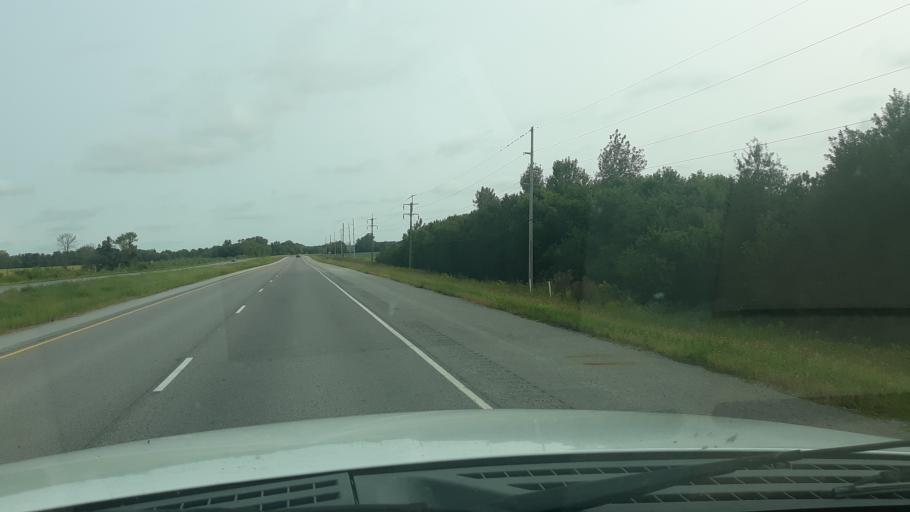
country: US
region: Illinois
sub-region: Saline County
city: Eldorado
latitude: 37.8684
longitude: -88.3988
